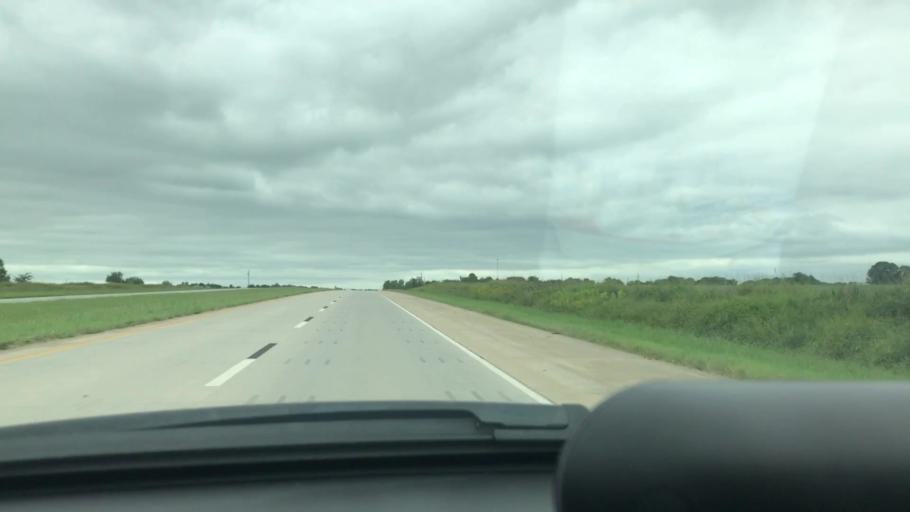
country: US
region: Oklahoma
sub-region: Mayes County
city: Chouteau
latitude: 36.0864
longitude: -95.3636
